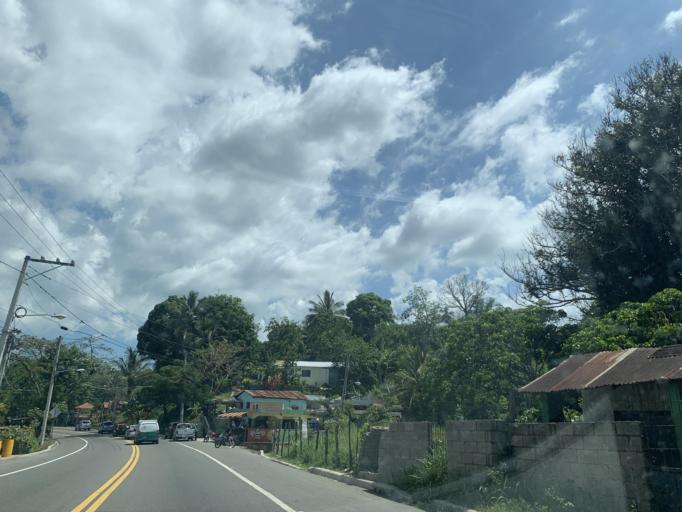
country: DO
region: Puerto Plata
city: Altamira
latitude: 19.6865
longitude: -70.8409
